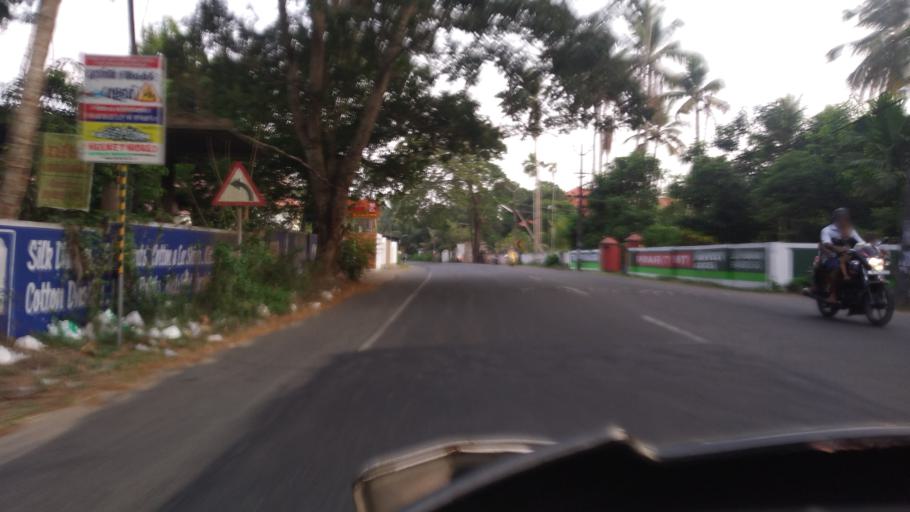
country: IN
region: Kerala
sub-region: Thrissur District
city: Kodungallur
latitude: 10.2493
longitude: 76.1863
